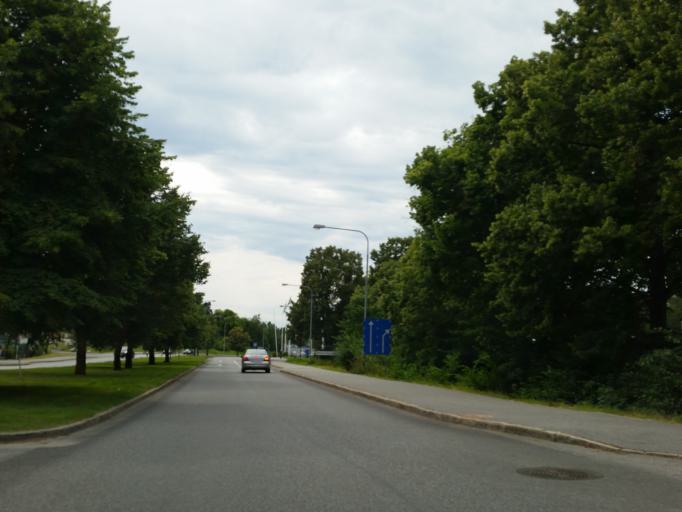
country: SE
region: Stockholm
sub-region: Sodertalje Kommun
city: Soedertaelje
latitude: 59.2064
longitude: 17.6467
